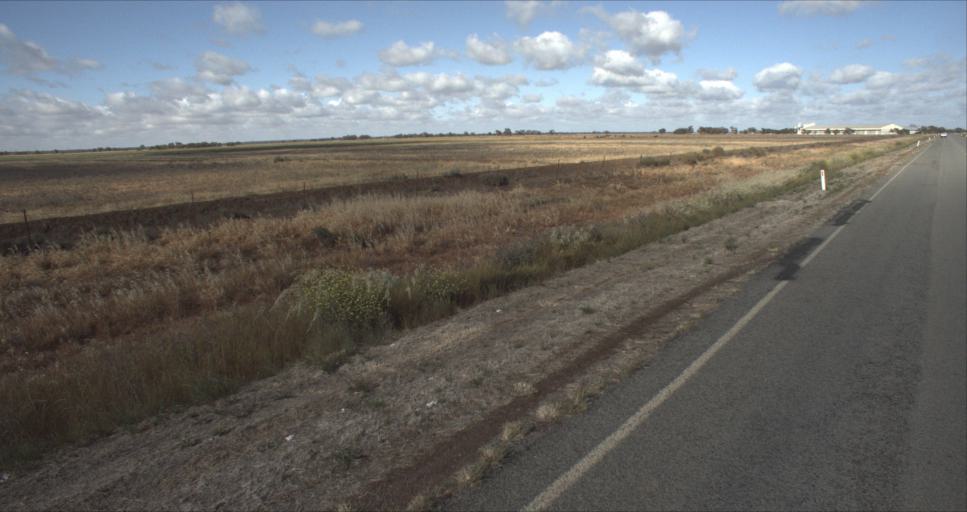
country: AU
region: New South Wales
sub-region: Leeton
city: Leeton
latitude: -34.5525
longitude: 146.2987
